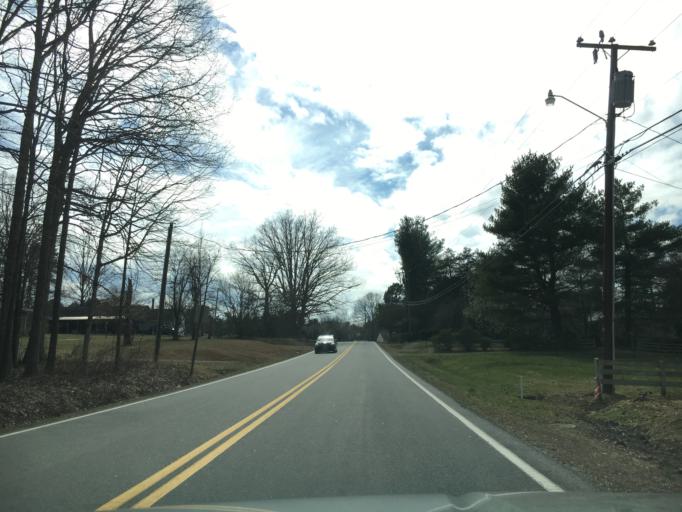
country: US
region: Virginia
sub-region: Halifax County
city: Halifax
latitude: 36.7482
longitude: -78.9248
